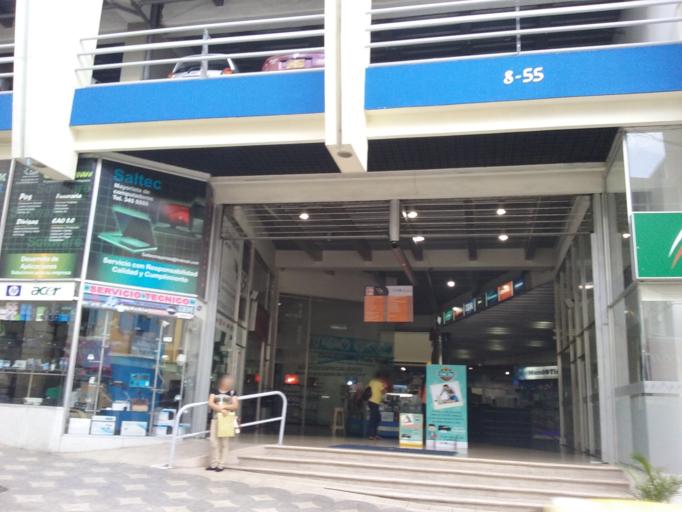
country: CO
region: Risaralda
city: Pereira
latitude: 4.8136
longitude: -75.6977
